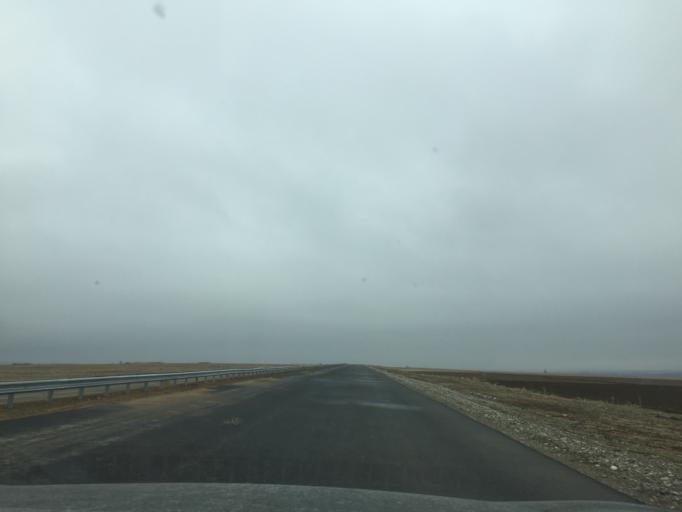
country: KZ
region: Ongtustik Qazaqstan
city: Kokterek
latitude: 42.5431
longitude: 70.2779
